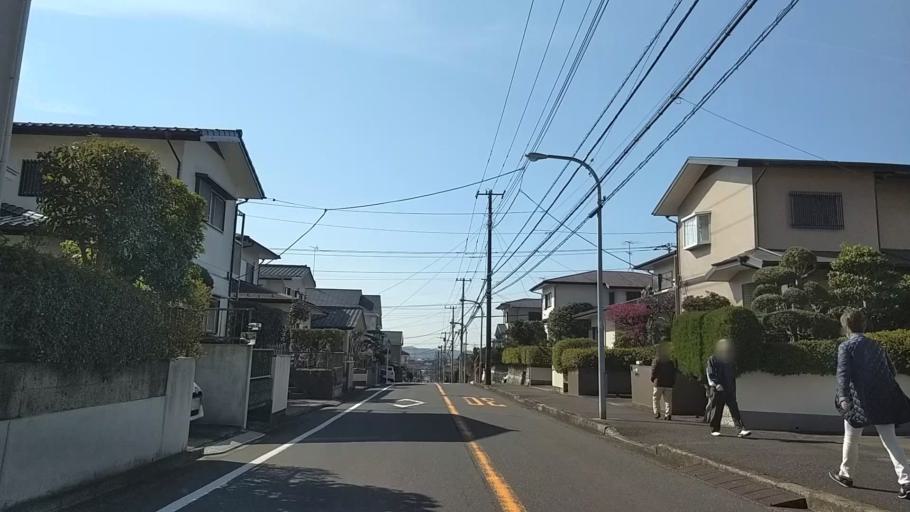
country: JP
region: Kanagawa
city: Kamakura
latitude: 35.3809
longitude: 139.5509
